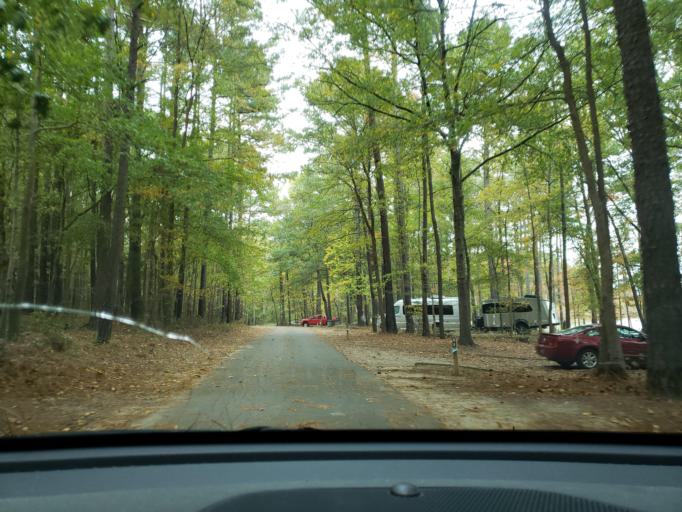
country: US
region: North Carolina
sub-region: Chatham County
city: Fearrington Village
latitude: 35.7424
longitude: -79.0342
